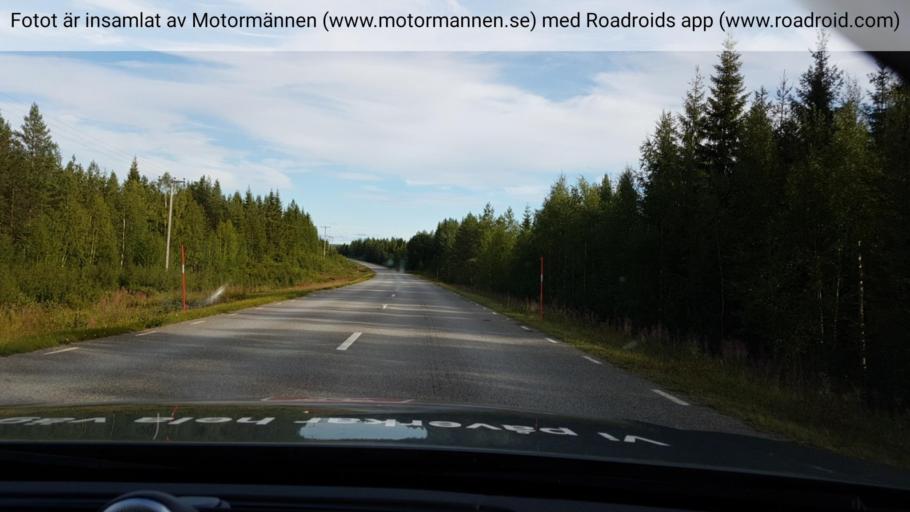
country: SE
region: Jaemtland
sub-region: Stroemsunds Kommun
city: Stroemsund
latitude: 64.2556
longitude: 15.4074
